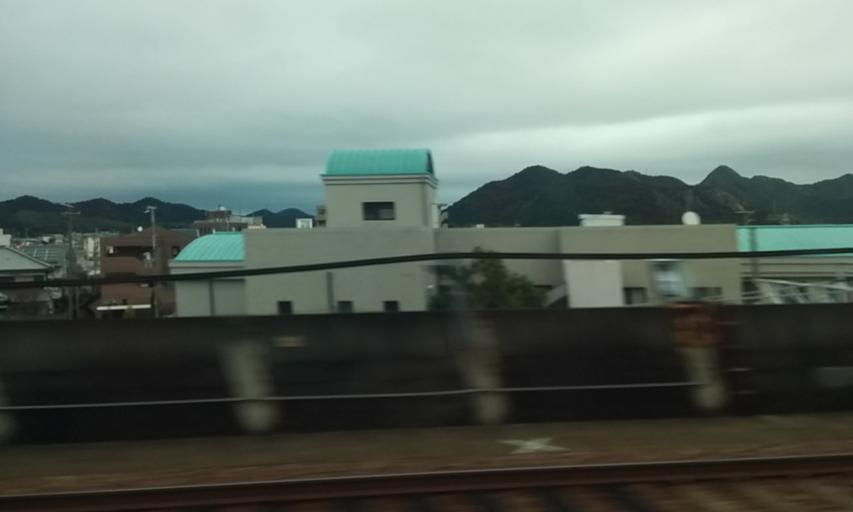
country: JP
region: Hyogo
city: Himeji
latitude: 34.8163
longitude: 134.7360
